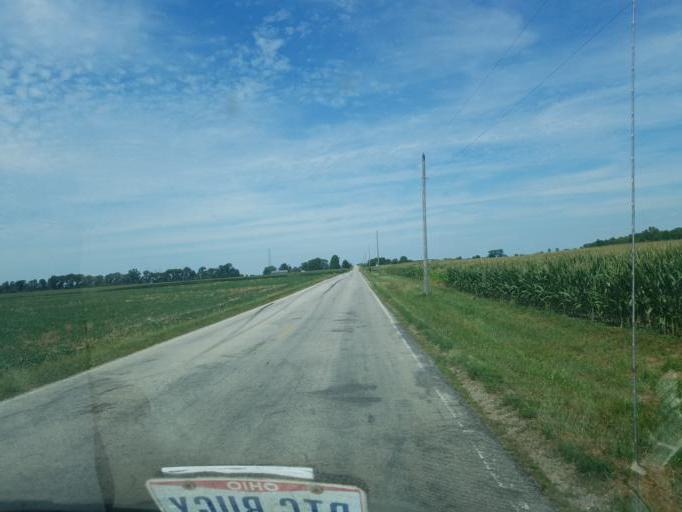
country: US
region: Ohio
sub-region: Madison County
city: West Jefferson
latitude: 39.9643
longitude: -83.2767
